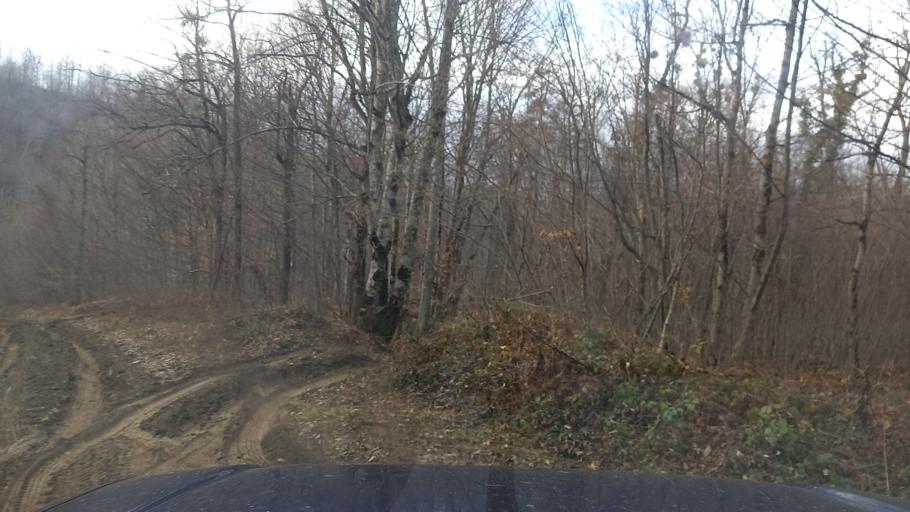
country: RU
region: Krasnodarskiy
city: Neftegorsk
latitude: 44.2013
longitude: 39.7012
